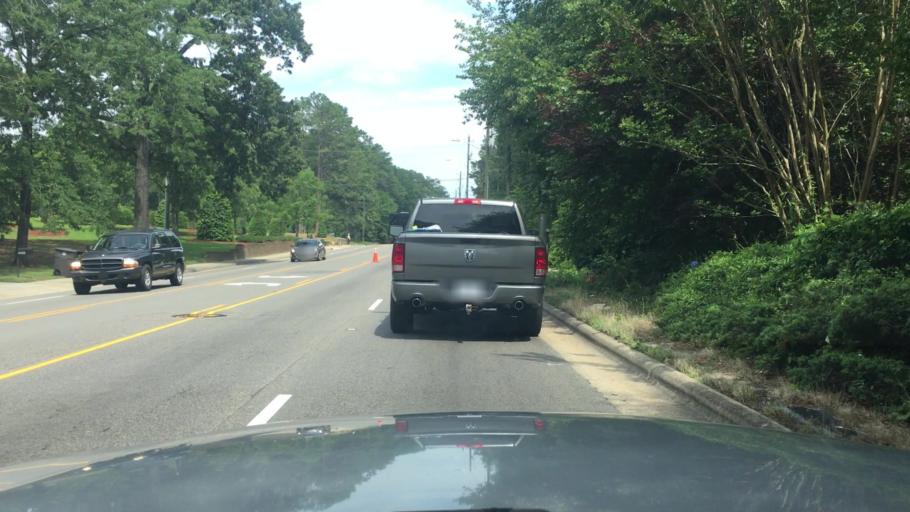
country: US
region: North Carolina
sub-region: Cumberland County
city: Fayetteville
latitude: 35.0639
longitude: -78.9248
